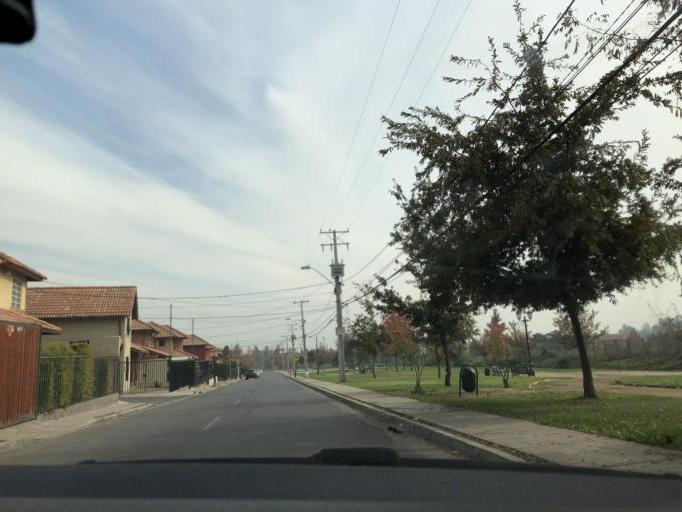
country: CL
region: Santiago Metropolitan
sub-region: Provincia de Cordillera
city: Puente Alto
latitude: -33.5558
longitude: -70.5481
